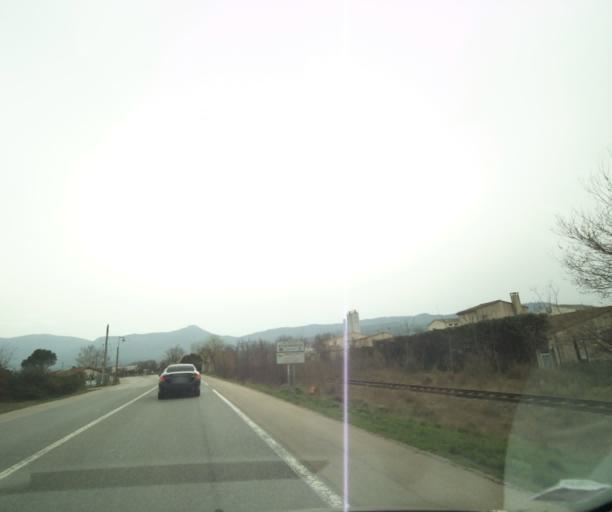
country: FR
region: Provence-Alpes-Cote d'Azur
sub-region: Departement des Bouches-du-Rhone
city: Trets
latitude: 43.4516
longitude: 5.6760
